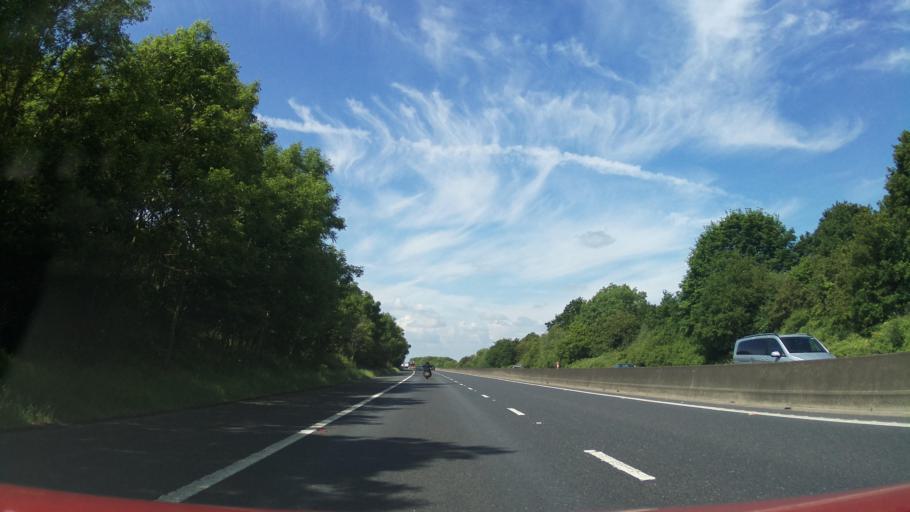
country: GB
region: England
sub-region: North Lincolnshire
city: Bottesford
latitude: 53.5463
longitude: -0.6297
